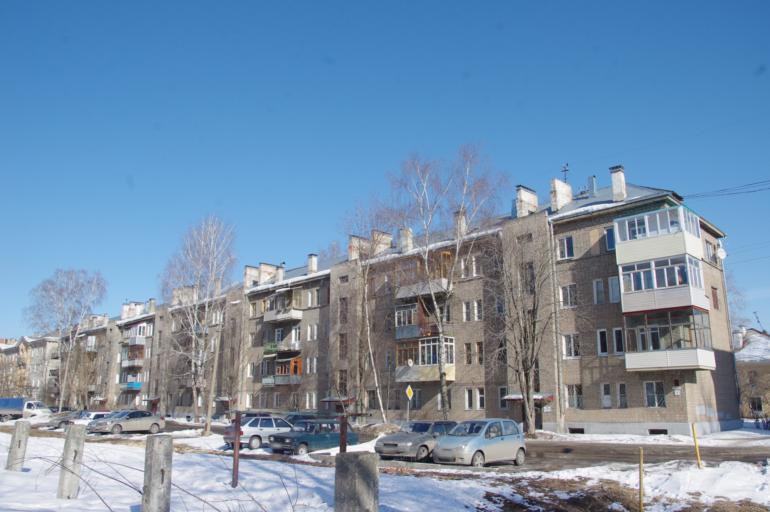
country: RU
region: Moskovskaya
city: Kolomna
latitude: 55.0767
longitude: 38.8045
